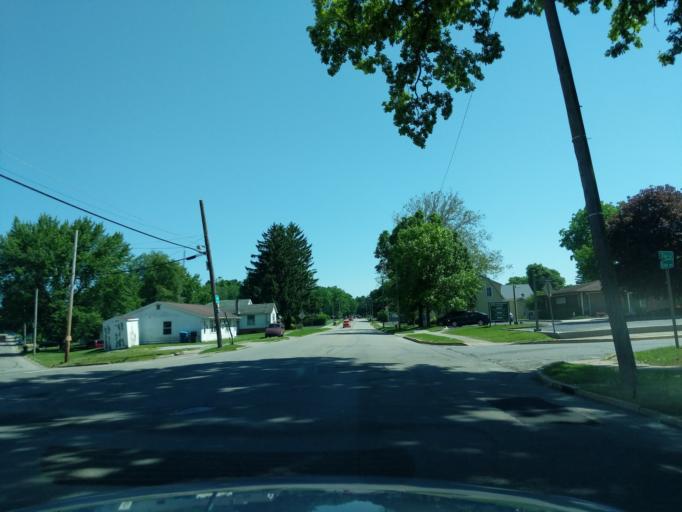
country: US
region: Indiana
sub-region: Huntington County
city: Huntington
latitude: 40.8696
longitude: -85.5007
